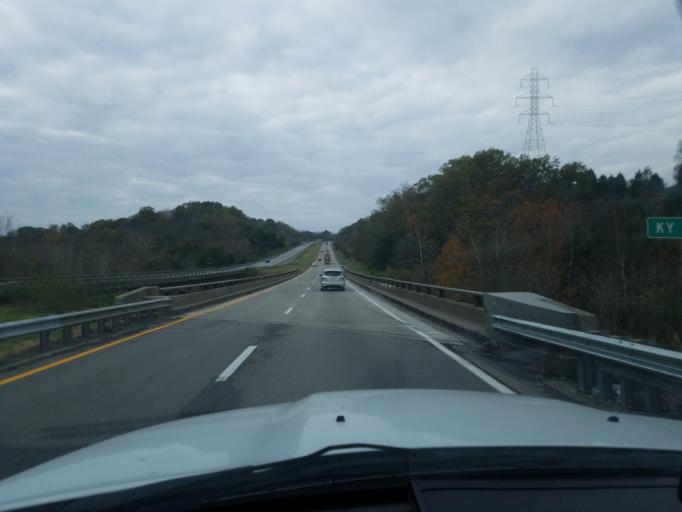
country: US
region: Indiana
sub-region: Switzerland County
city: Vevay
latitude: 38.6551
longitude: -85.0775
